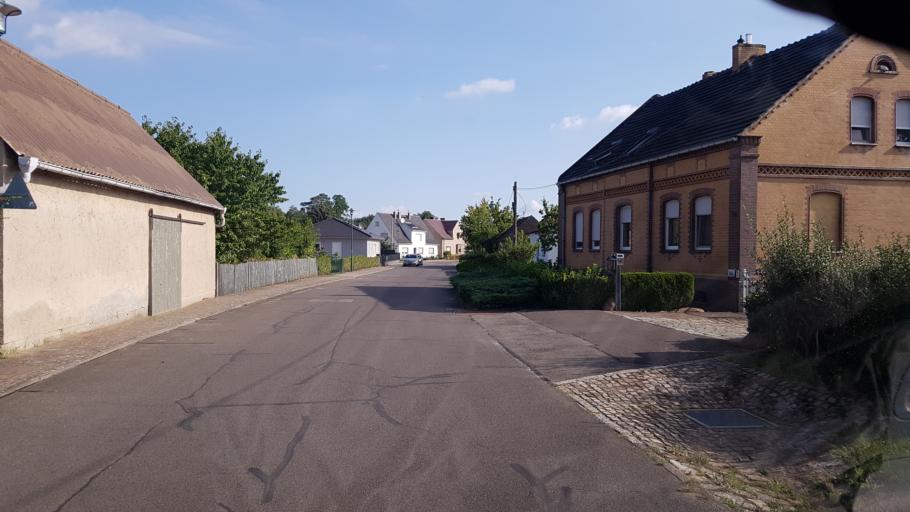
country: DE
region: Brandenburg
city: Luebben
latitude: 51.8848
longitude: 13.8451
